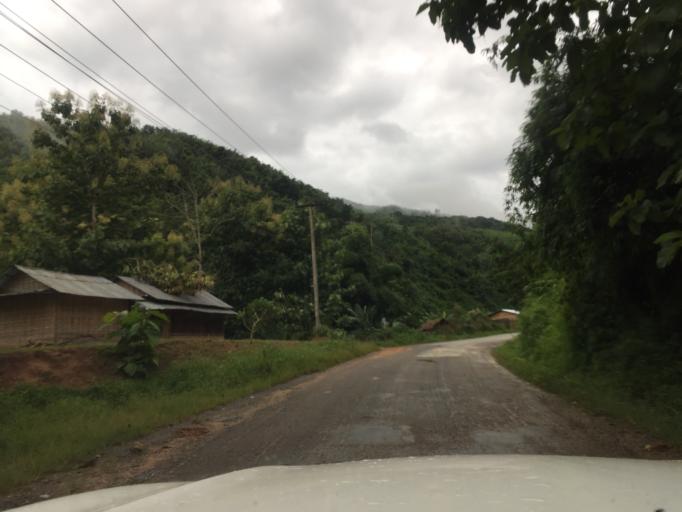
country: LA
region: Oudomxai
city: Muang La
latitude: 20.9768
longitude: 102.2235
